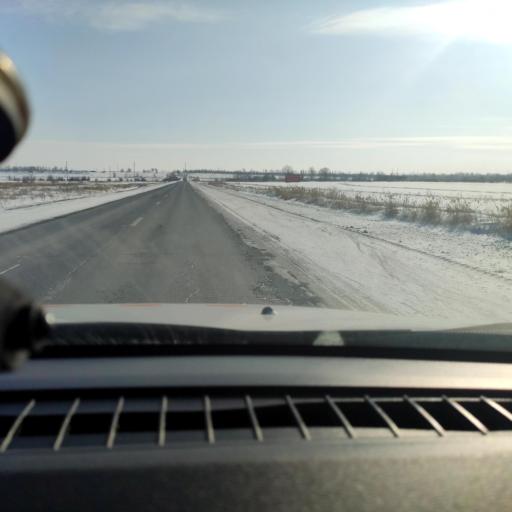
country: RU
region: Samara
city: Smyshlyayevka
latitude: 53.1638
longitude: 50.4570
